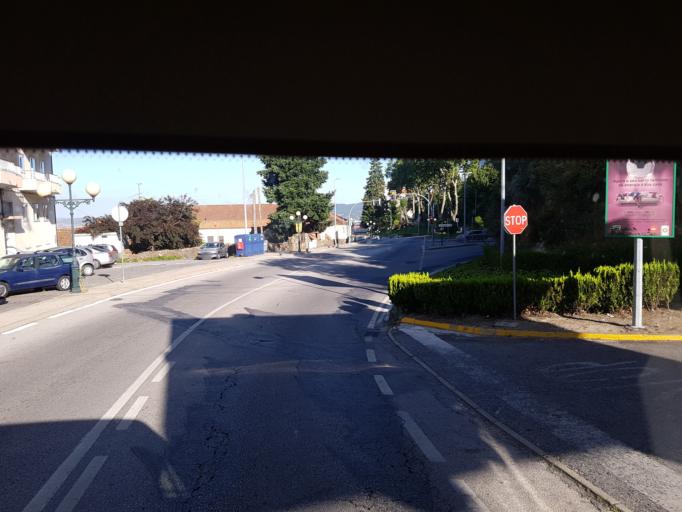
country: PT
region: Castelo Branco
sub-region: Covilha
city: Covilha
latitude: 40.2758
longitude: -7.5055
